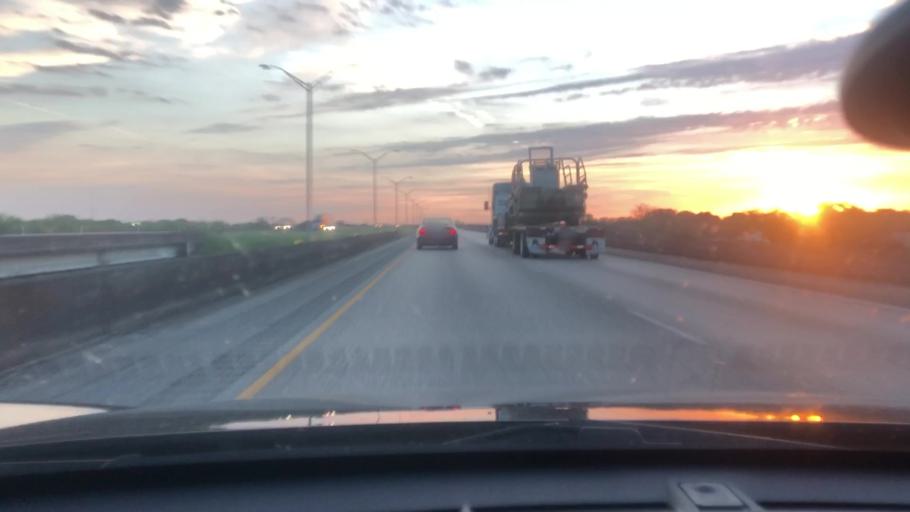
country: US
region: Texas
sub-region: Jackson County
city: Edna
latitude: 28.9861
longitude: -96.6521
